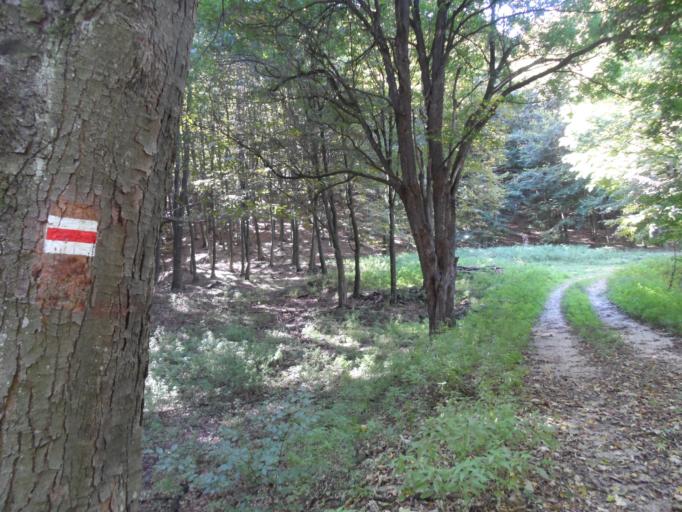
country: HU
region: Veszprem
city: Herend
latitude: 47.2655
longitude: 17.6907
